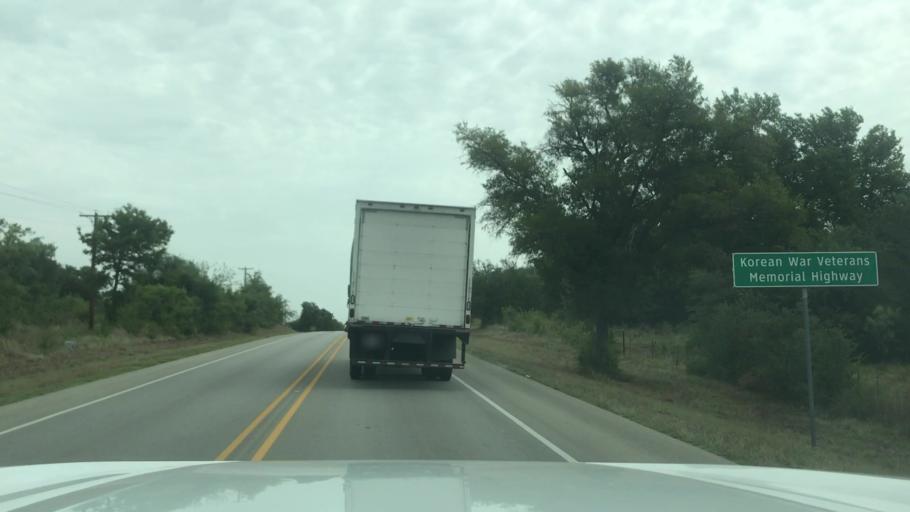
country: US
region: Texas
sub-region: Erath County
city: Dublin
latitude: 32.0890
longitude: -98.4261
